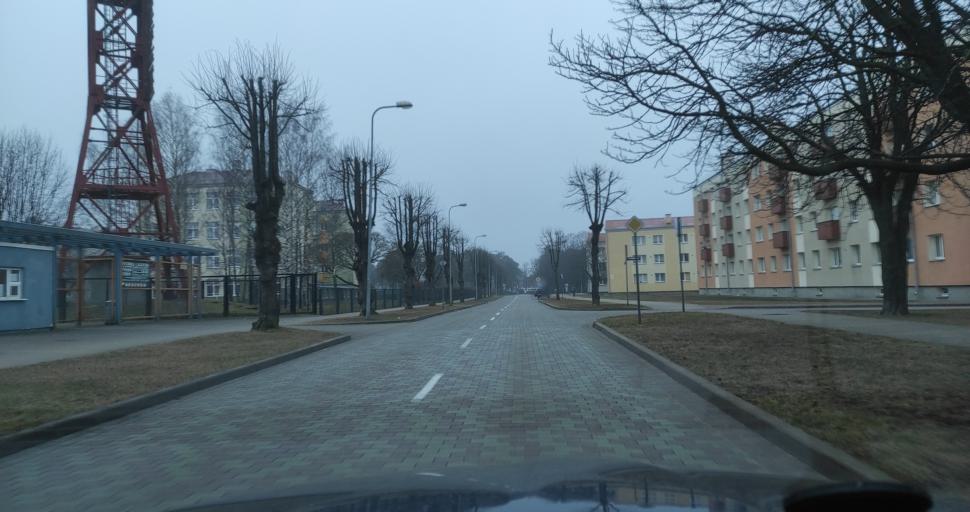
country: LV
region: Ventspils
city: Ventspils
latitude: 57.3881
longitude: 21.5520
